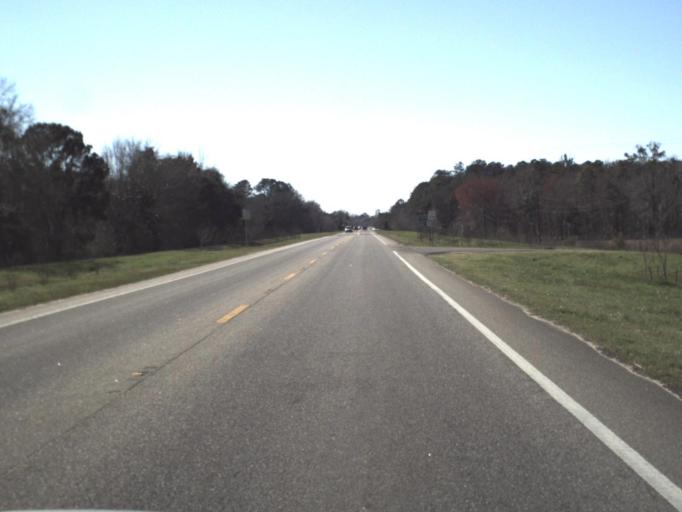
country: US
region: Florida
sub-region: Calhoun County
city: Blountstown
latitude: 30.4432
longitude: -85.0320
